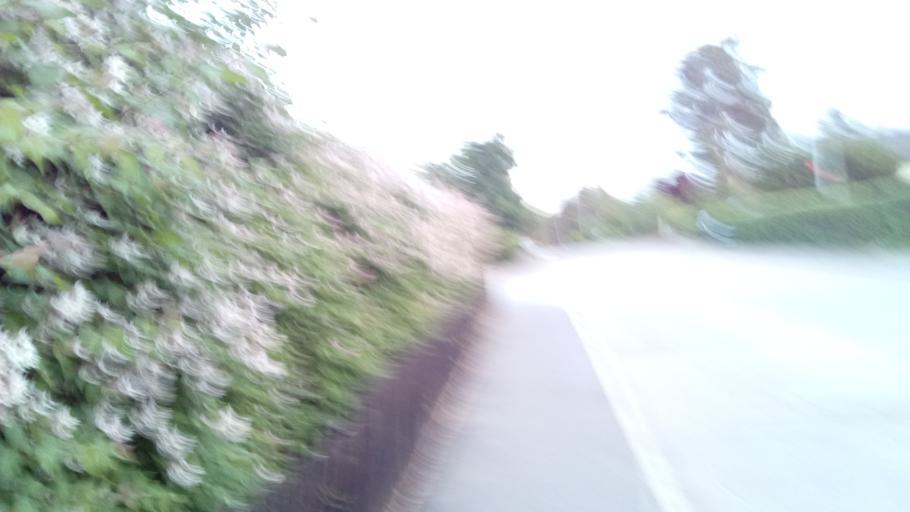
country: SE
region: Stockholm
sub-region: Tyreso Kommun
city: Bollmora
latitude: 59.2425
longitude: 18.2486
